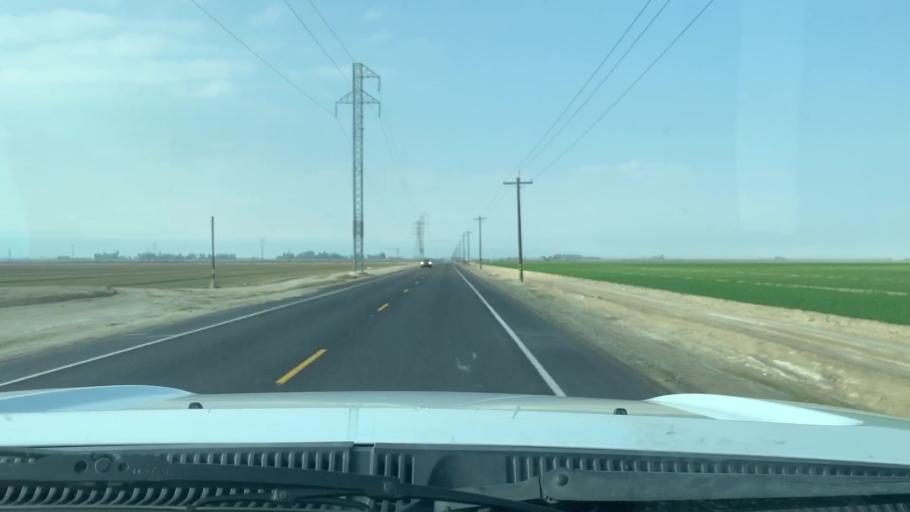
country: US
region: California
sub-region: Kern County
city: Buttonwillow
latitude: 35.4421
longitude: -119.3712
